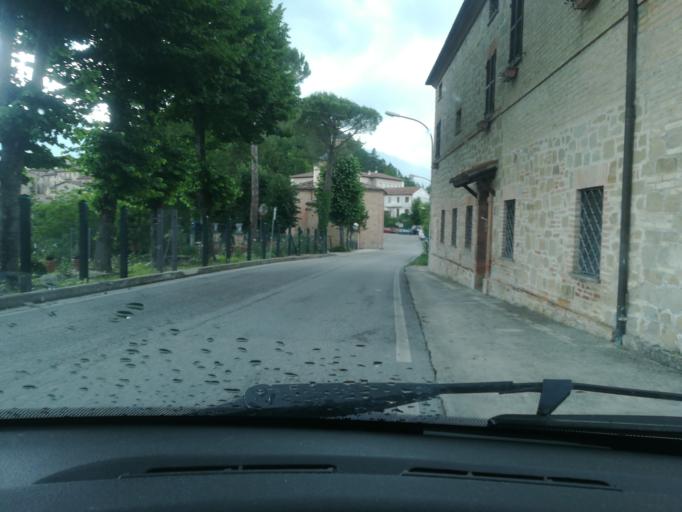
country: IT
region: The Marches
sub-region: Province of Fermo
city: Montefortino
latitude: 42.9426
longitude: 13.3463
